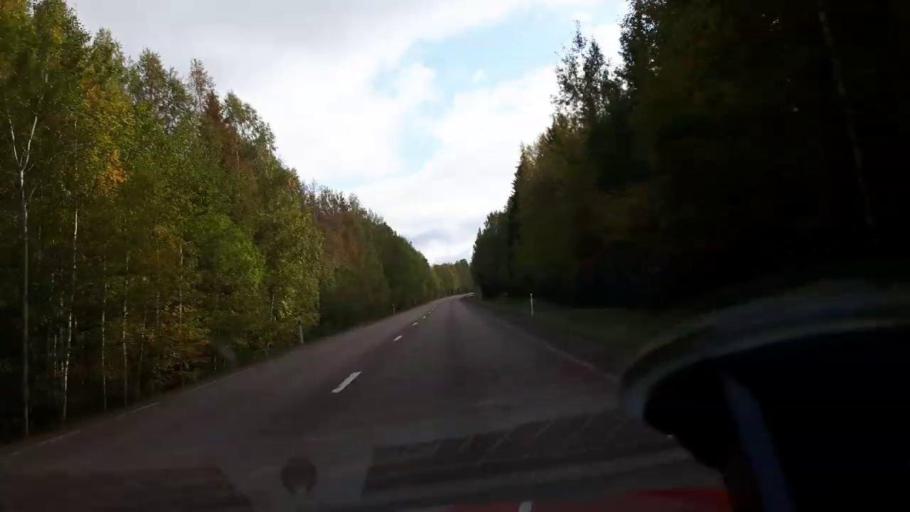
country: SE
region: Gaevleborg
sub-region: Ljusdals Kommun
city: Jaervsoe
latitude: 61.6448
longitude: 16.2139
